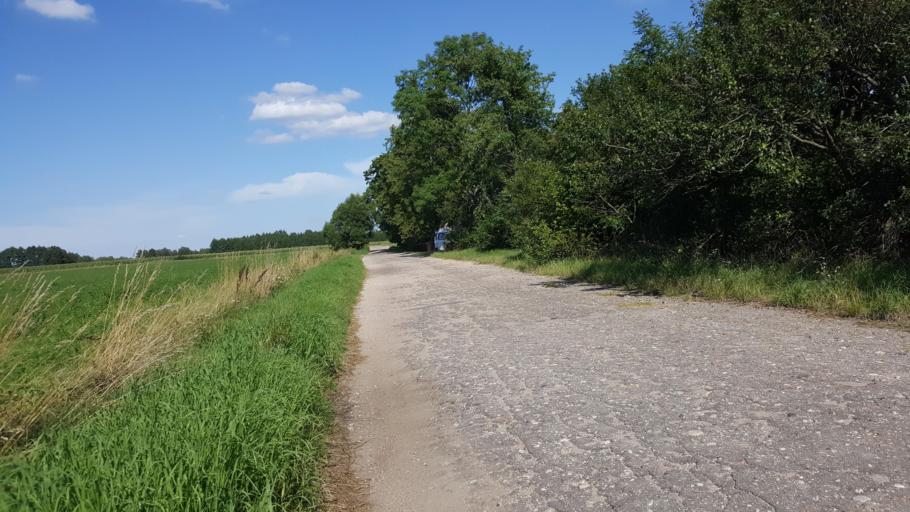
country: BY
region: Brest
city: Charnawchytsy
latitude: 52.3284
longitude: 23.6418
